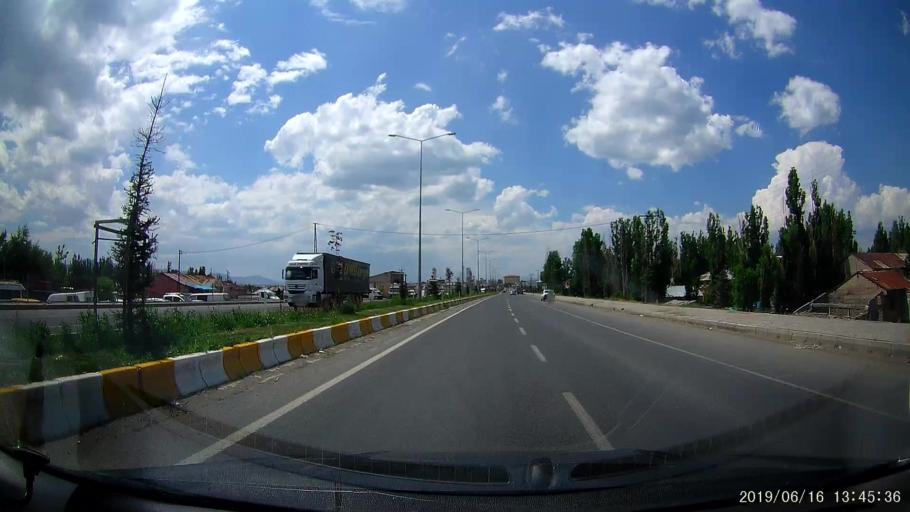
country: TR
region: Agri
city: Agri
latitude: 39.7094
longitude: 43.0435
